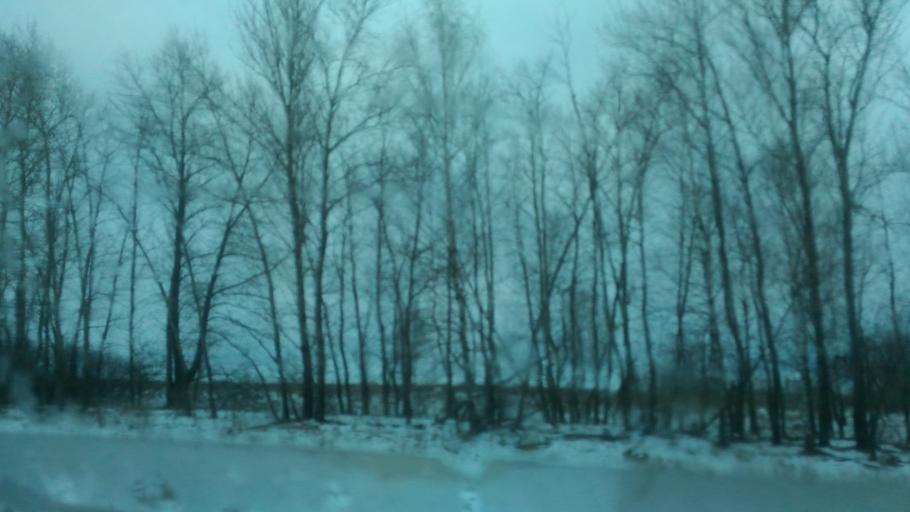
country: RU
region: Tula
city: Bolokhovo
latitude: 54.0746
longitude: 37.7896
